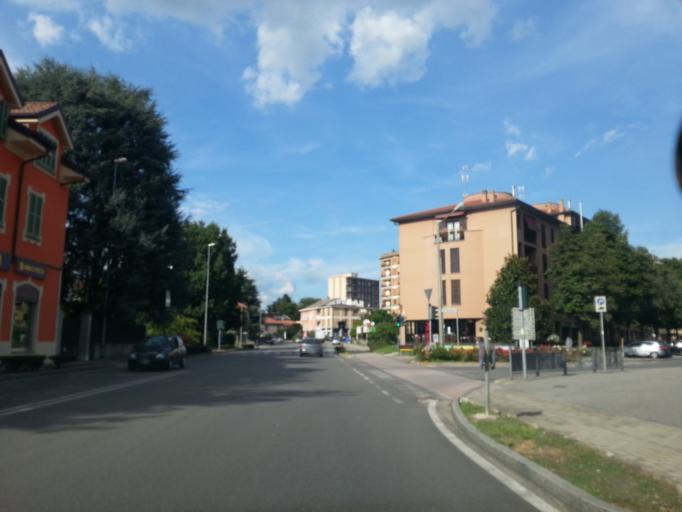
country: IT
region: Lombardy
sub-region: Provincia di Monza e Brianza
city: Vedano al Lambro
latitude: 45.6101
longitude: 9.2711
